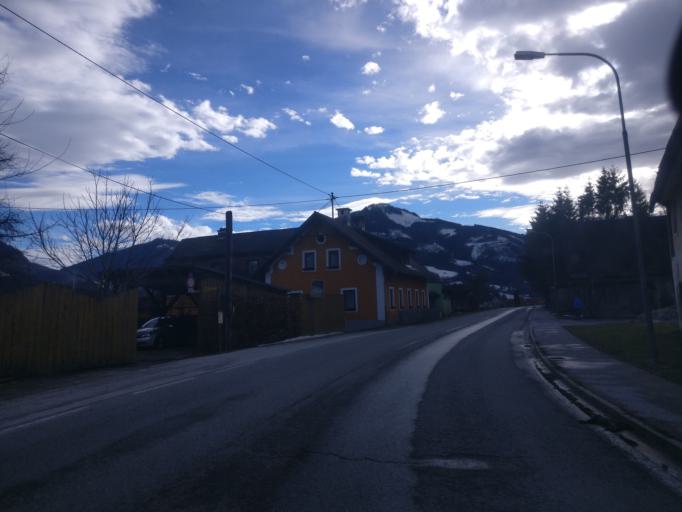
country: AT
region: Styria
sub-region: Politischer Bezirk Liezen
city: Hall bei Admont
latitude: 47.5872
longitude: 14.4702
